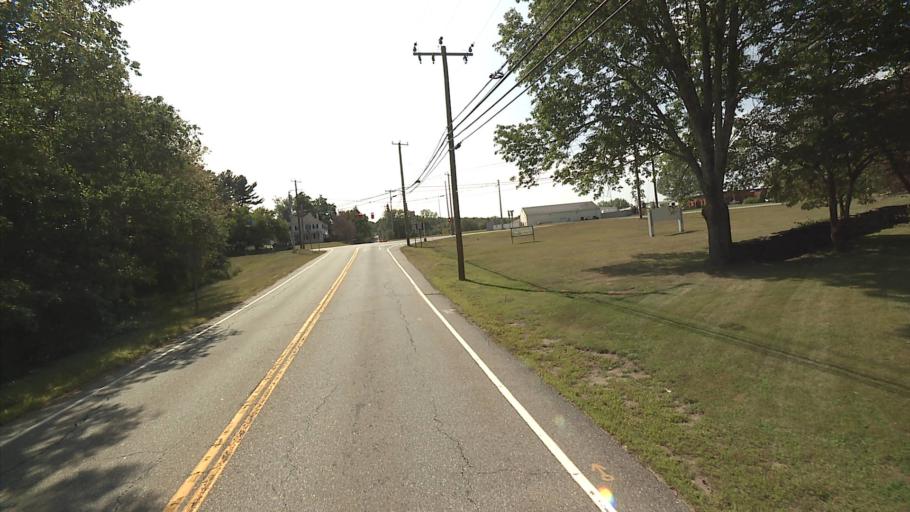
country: US
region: Connecticut
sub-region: Windham County
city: Putnam
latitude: 41.8586
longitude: -71.9592
